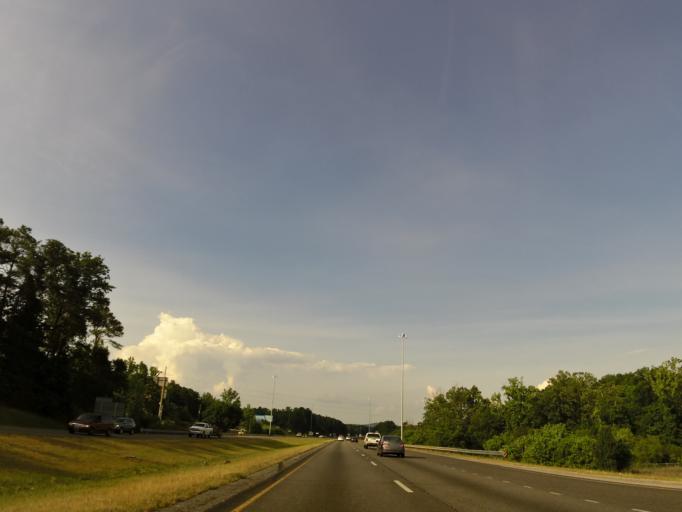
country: US
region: Alabama
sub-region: Jefferson County
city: Trussville
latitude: 33.6434
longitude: -86.6141
